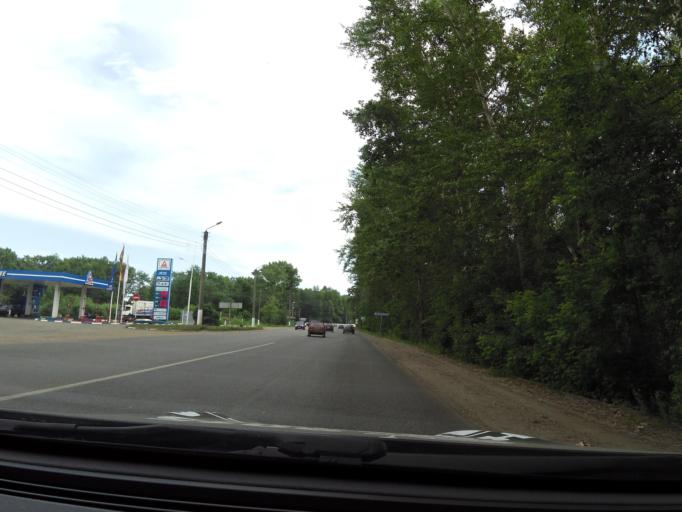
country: RU
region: Kirov
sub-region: Kirovo-Chepetskiy Rayon
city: Kirov
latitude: 58.6163
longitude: 49.7377
